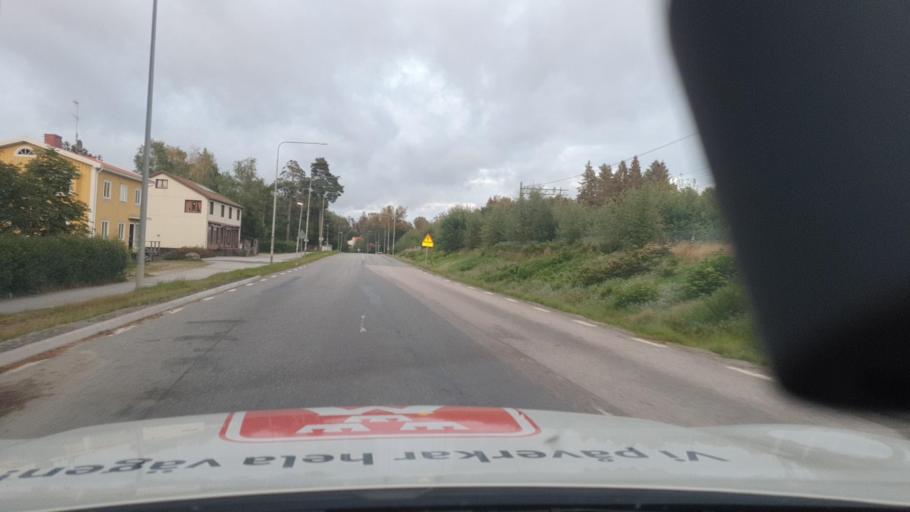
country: SE
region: Vaestra Goetaland
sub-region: Harryda Kommun
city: Hindas
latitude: 57.7047
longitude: 12.4517
